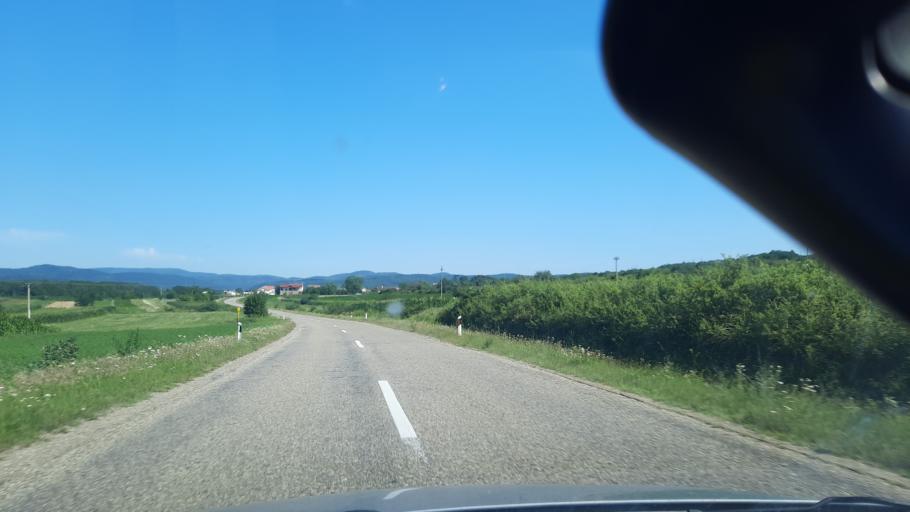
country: RS
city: Turija
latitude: 44.5581
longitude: 21.5382
